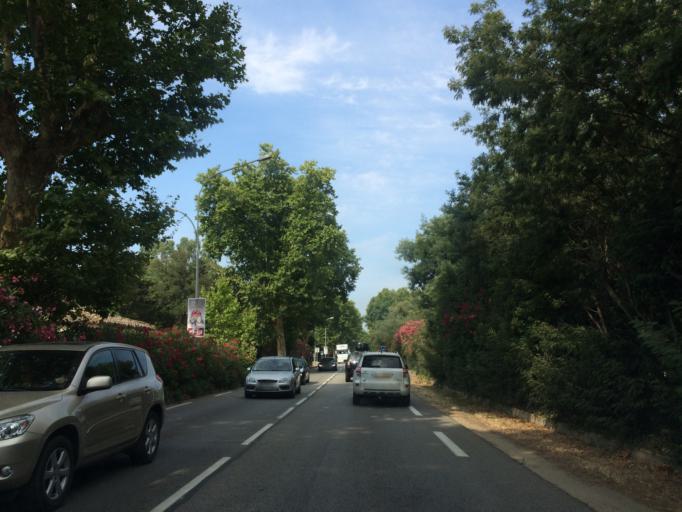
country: FR
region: Provence-Alpes-Cote d'Azur
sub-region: Departement du Var
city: Gassin
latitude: 43.2824
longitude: 6.5867
